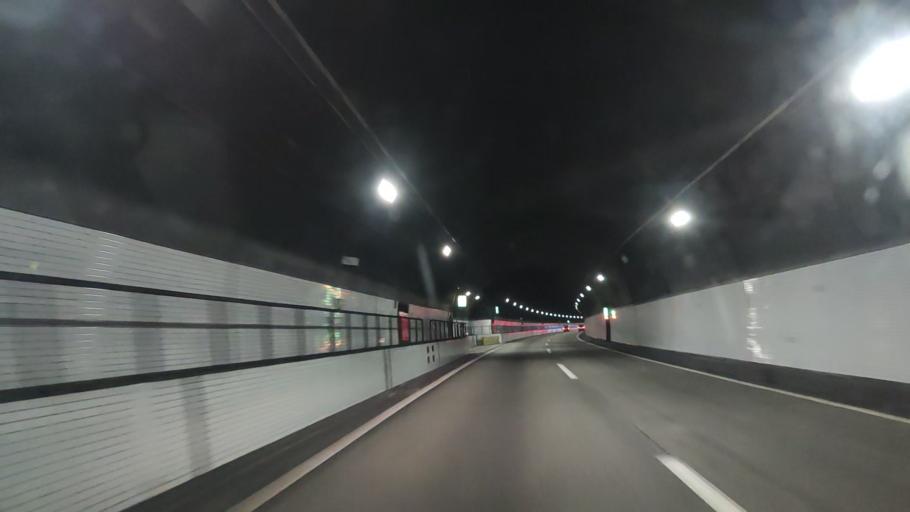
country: JP
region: Ehime
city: Niihama
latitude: 33.9161
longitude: 133.3060
